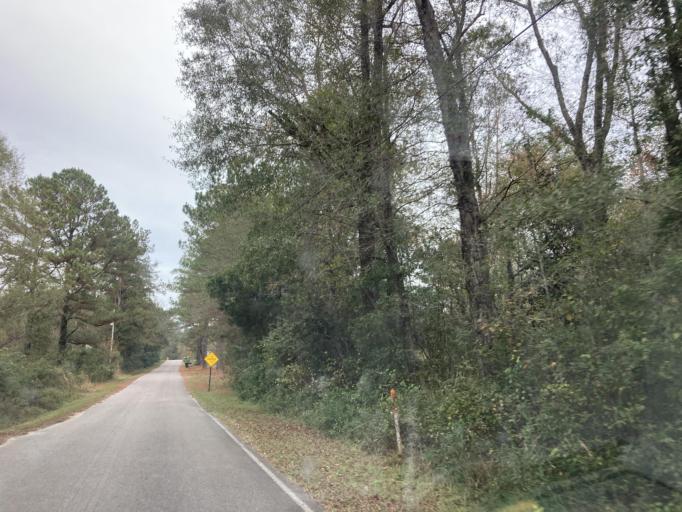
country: US
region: Mississippi
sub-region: Lamar County
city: Purvis
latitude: 31.0735
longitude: -89.4297
